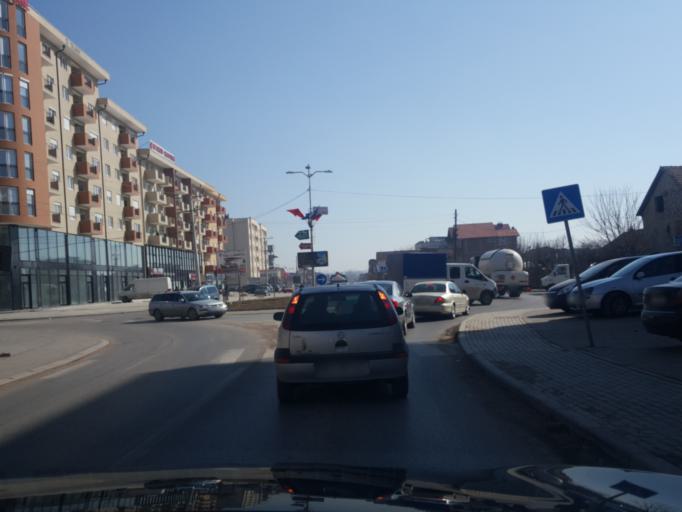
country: XK
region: Mitrovica
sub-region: Vushtrri
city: Vushtrri
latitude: 42.8270
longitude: 20.9699
